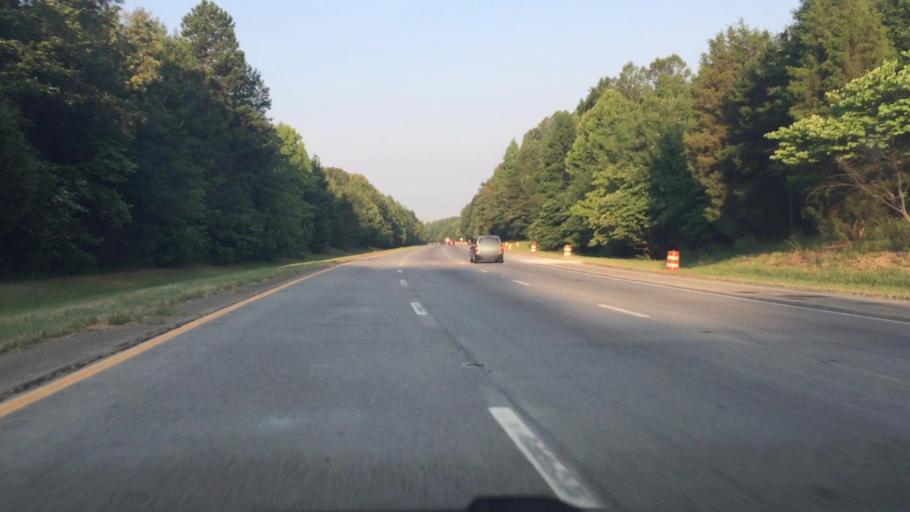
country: US
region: North Carolina
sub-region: Davidson County
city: Thomasville
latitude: 35.8354
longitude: -80.1363
